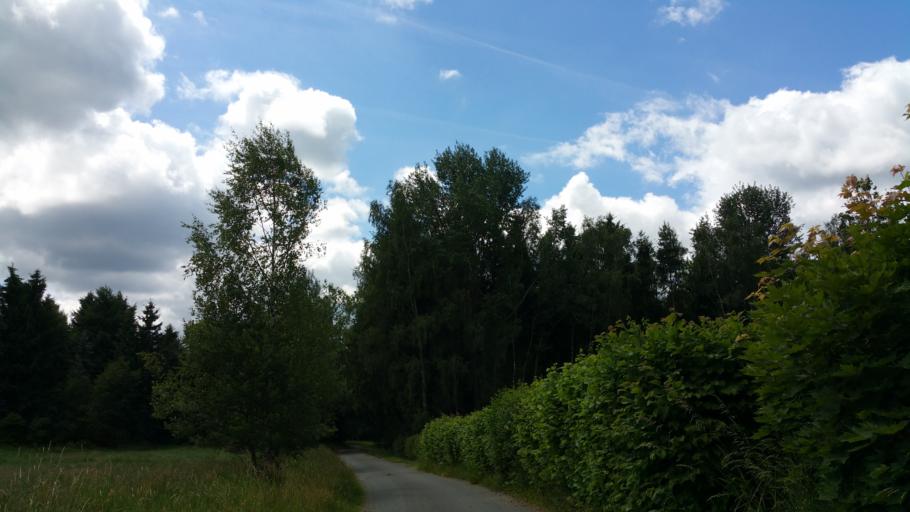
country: DE
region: Bavaria
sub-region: Upper Franconia
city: Schwarzenbach an der Saale
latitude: 50.2117
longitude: 11.9295
